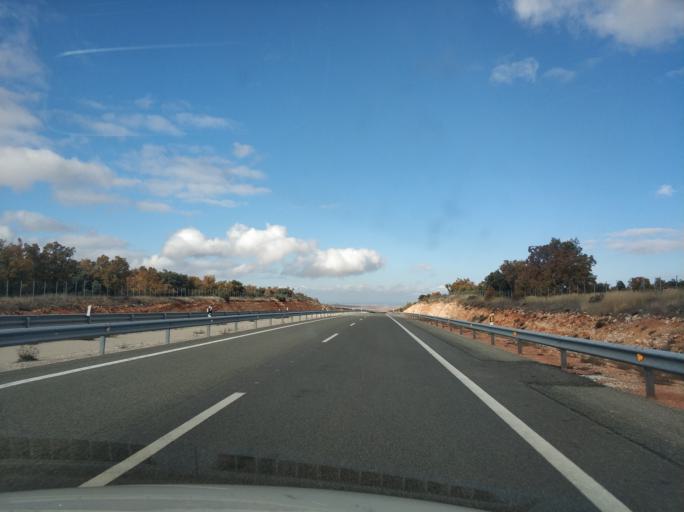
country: ES
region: Castille and Leon
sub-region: Provincia de Soria
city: Adradas
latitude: 41.3058
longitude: -2.4803
